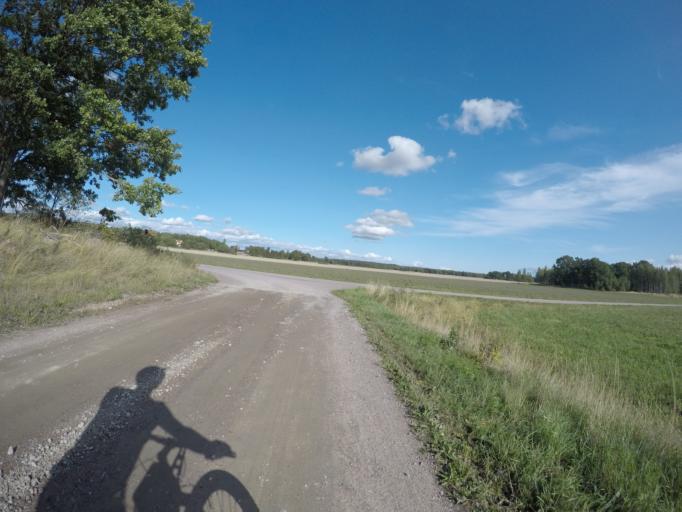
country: SE
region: Soedermanland
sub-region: Eskilstuna Kommun
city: Kvicksund
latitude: 59.5089
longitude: 16.3458
